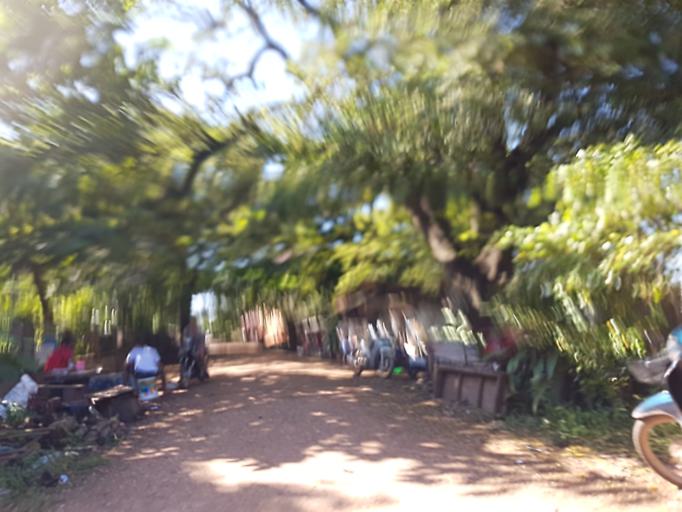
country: TH
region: Nong Khai
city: Si Chiang Mai
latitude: 17.9180
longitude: 102.6163
